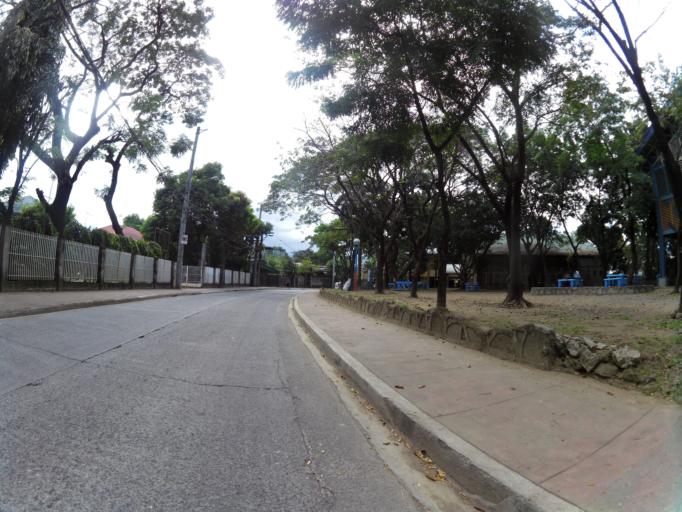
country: PH
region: Metro Manila
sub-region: Marikina
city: Calumpang
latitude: 14.6259
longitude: 121.1037
